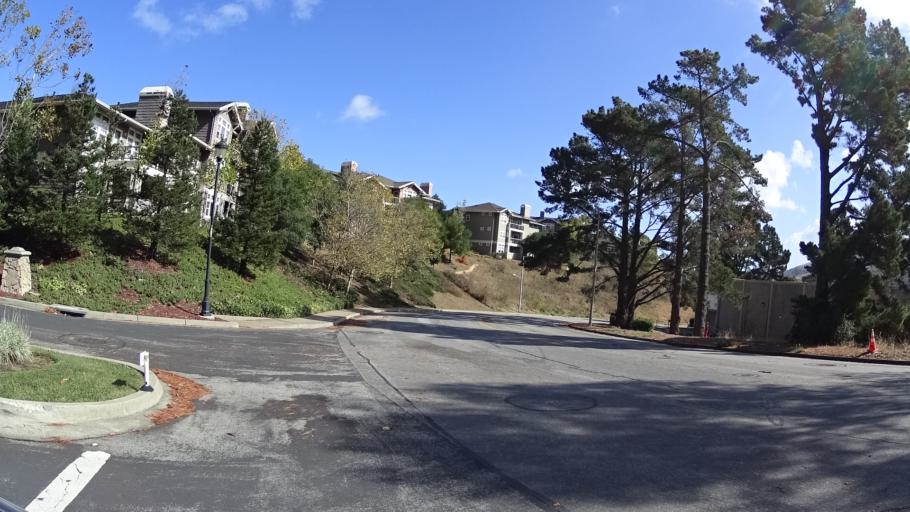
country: US
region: California
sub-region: San Mateo County
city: Brisbane
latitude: 37.6934
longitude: -122.4208
